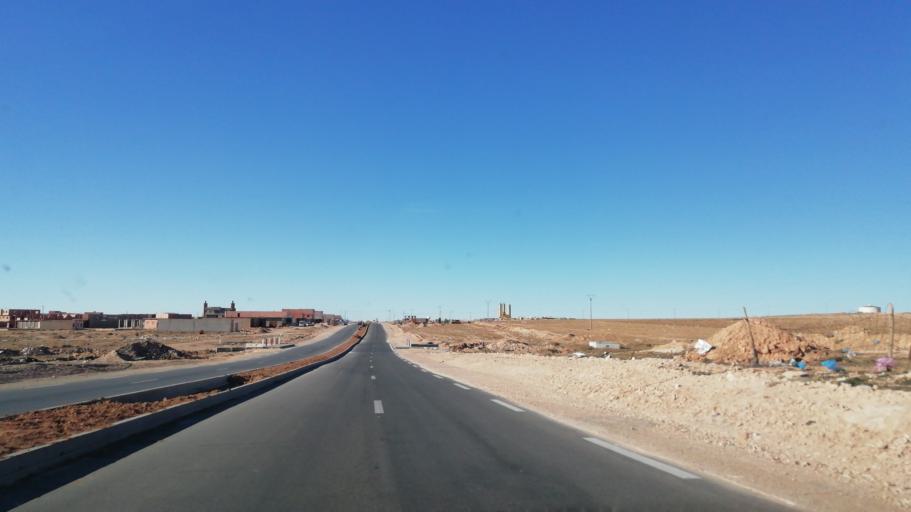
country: DZ
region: Tlemcen
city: Sebdou
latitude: 34.2147
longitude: -1.2441
